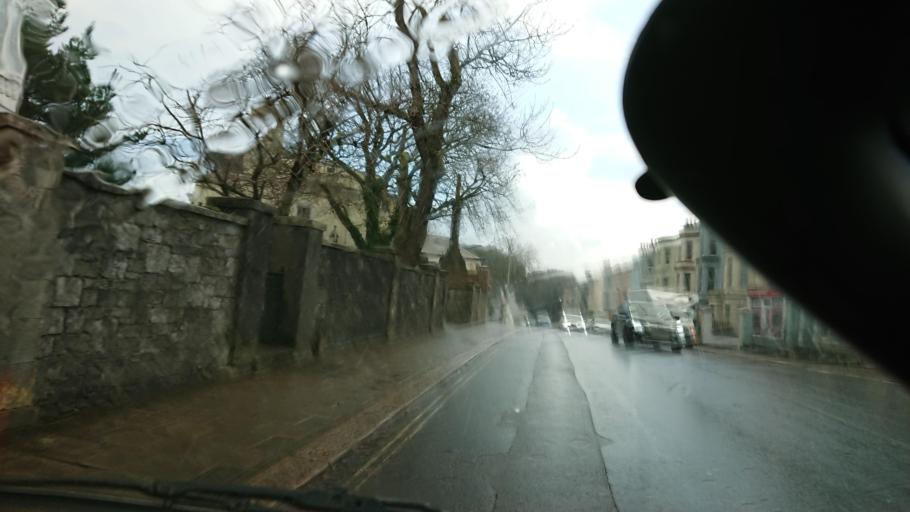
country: GB
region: England
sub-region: Cornwall
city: Millbrook
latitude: 50.3775
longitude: -4.1683
